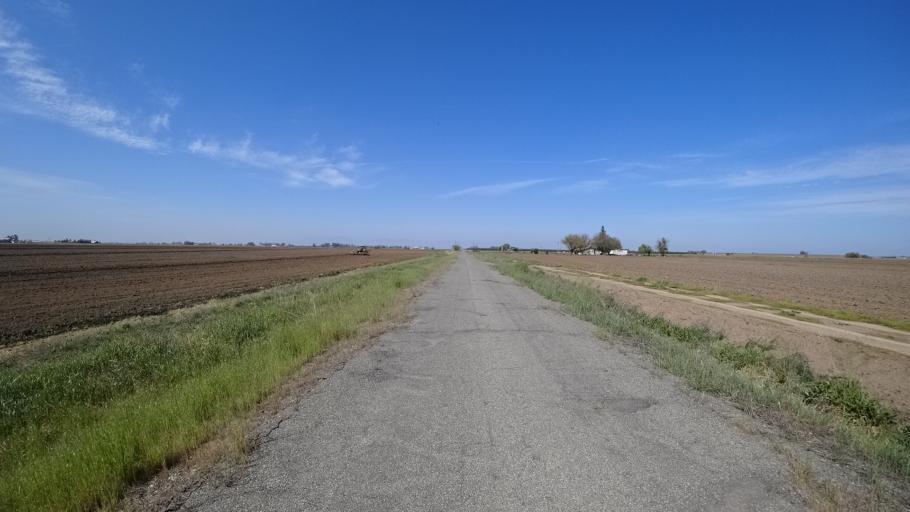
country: US
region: California
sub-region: Glenn County
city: Hamilton City
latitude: 39.6088
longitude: -122.0284
